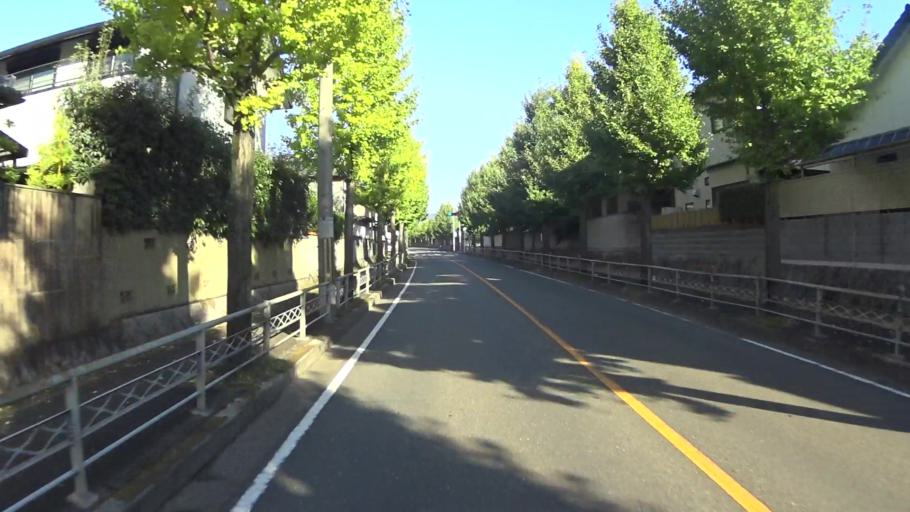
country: JP
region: Kyoto
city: Muko
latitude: 34.9563
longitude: 135.6869
